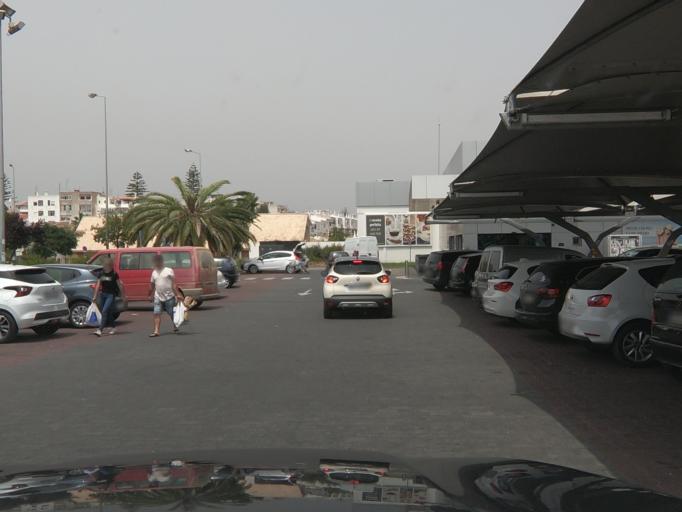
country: PT
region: Faro
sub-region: Portimao
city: Portimao
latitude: 37.1339
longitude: -8.5461
